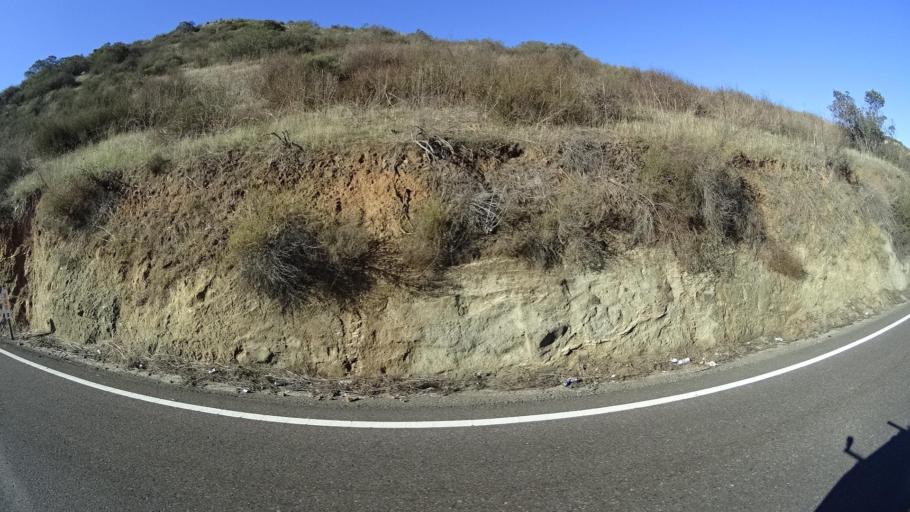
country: US
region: California
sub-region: San Diego County
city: Jamul
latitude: 32.6498
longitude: -116.7868
